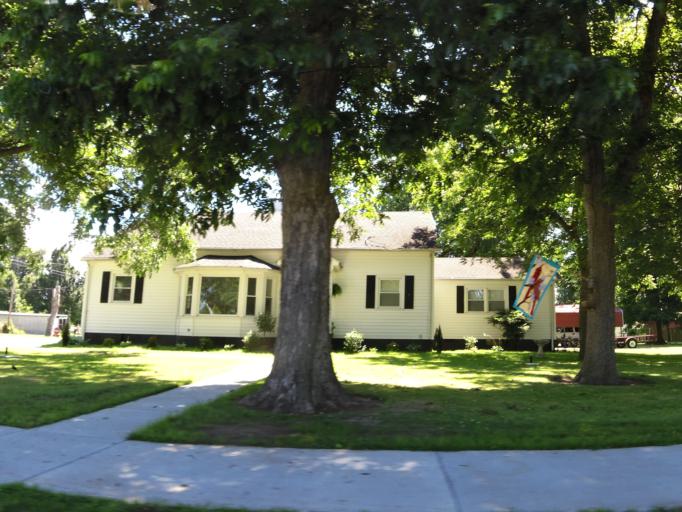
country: US
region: Missouri
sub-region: New Madrid County
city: New Madrid
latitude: 36.5949
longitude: -89.5273
